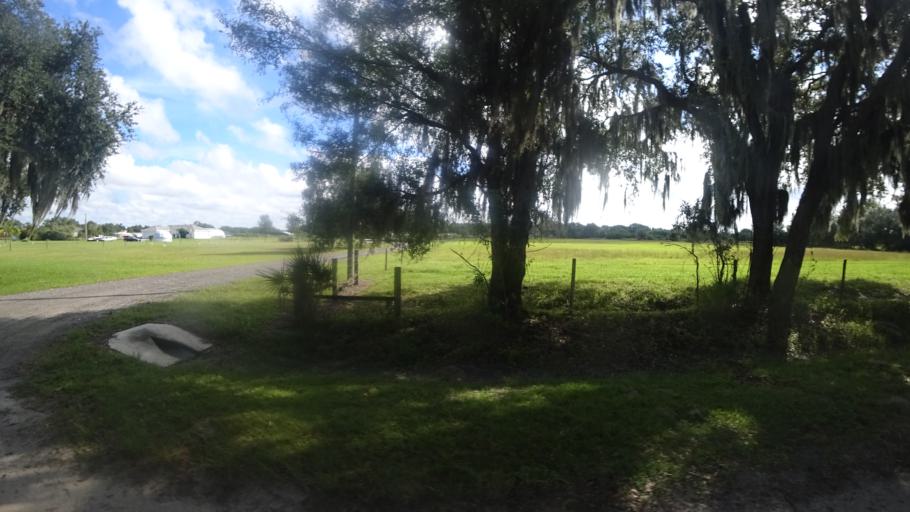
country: US
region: Florida
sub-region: Hillsborough County
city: Ruskin
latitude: 27.6387
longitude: -82.4171
